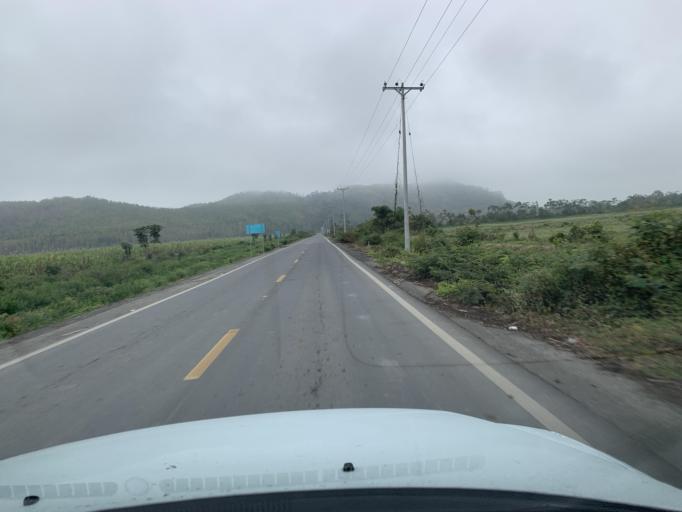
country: EC
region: Guayas
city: Coronel Marcelino Mariduena
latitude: -2.3455
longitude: -79.5294
